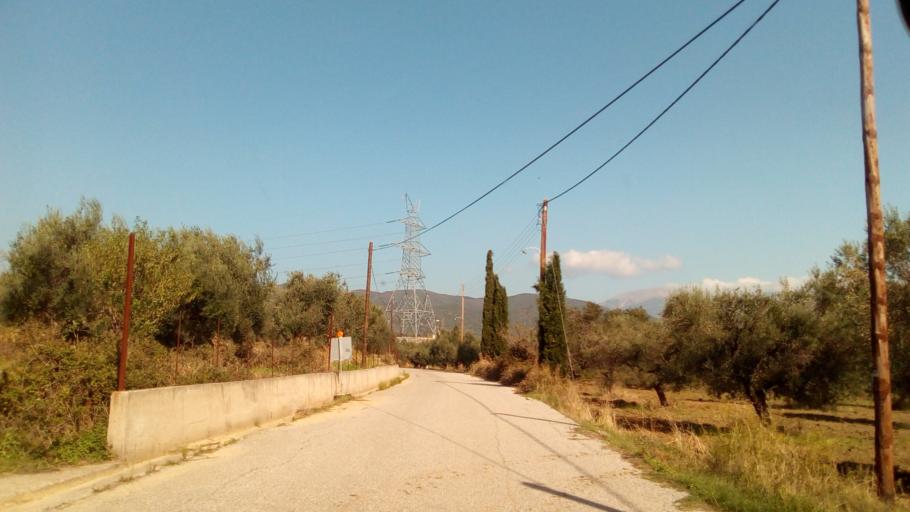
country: GR
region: West Greece
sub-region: Nomos Aitolias kai Akarnanias
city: Antirrio
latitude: 38.3431
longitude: 21.7617
